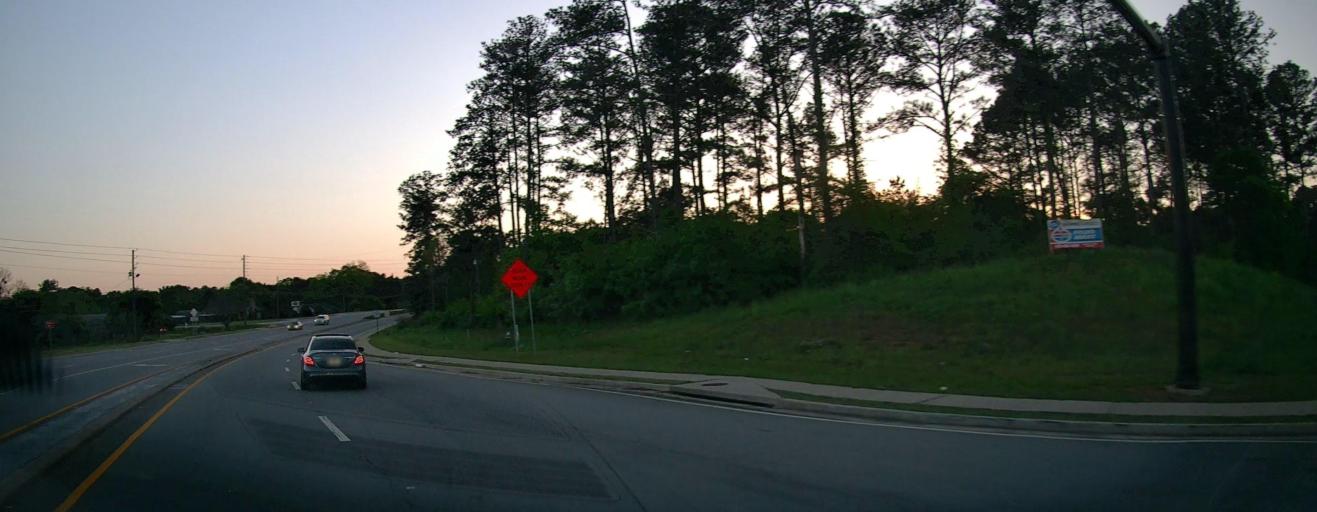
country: US
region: Georgia
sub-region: Henry County
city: McDonough
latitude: 33.4835
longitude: -84.1965
